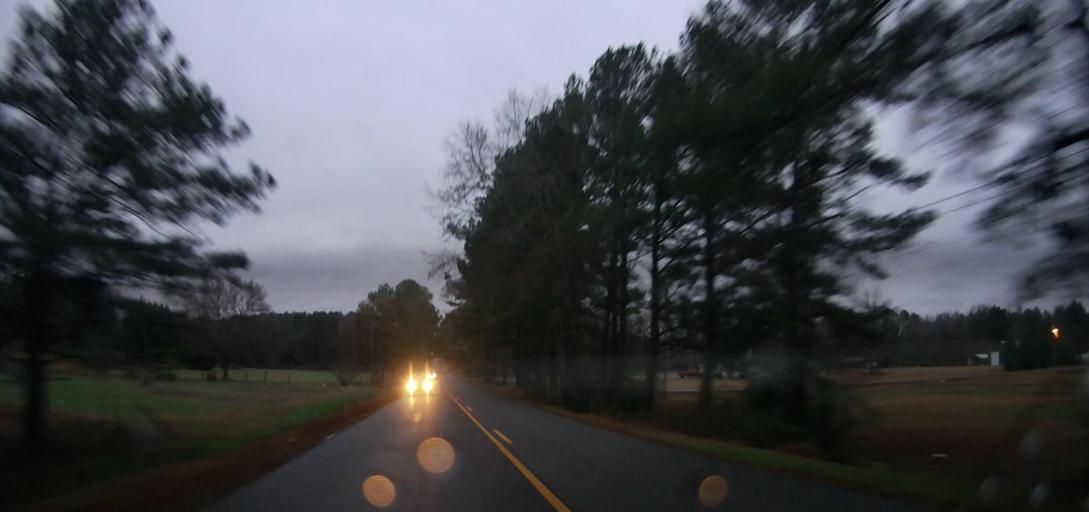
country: US
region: Alabama
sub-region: Tuscaloosa County
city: Vance
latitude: 33.1409
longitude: -87.2298
